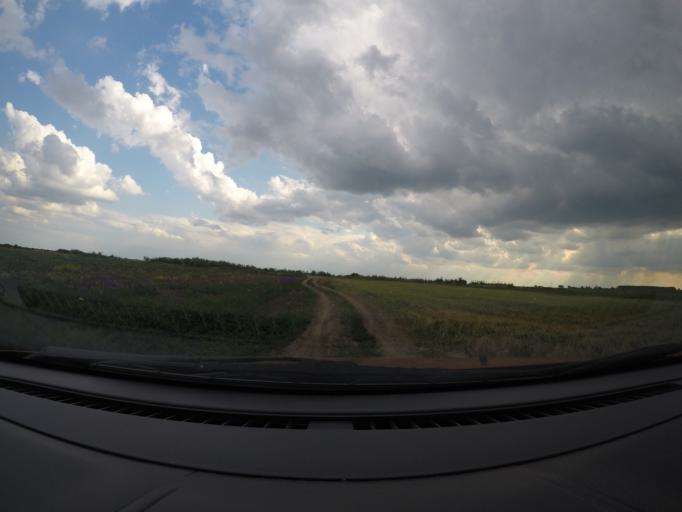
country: RS
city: Uzdin
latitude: 45.2038
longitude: 20.6003
